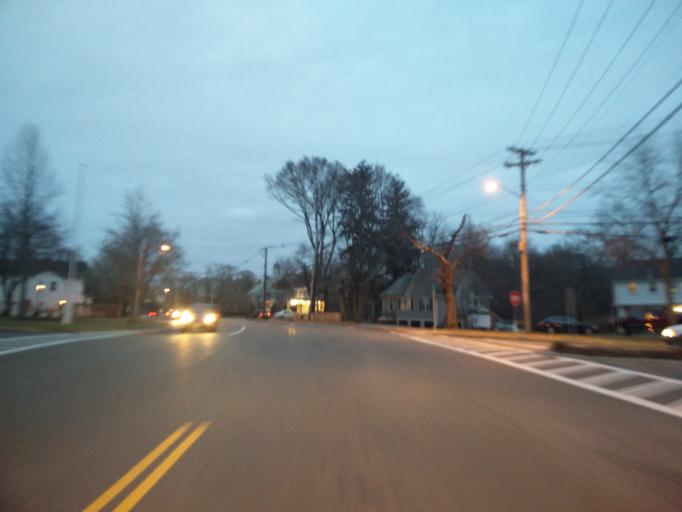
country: US
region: Massachusetts
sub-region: Plymouth County
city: Hingham
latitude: 42.2328
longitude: -70.8798
